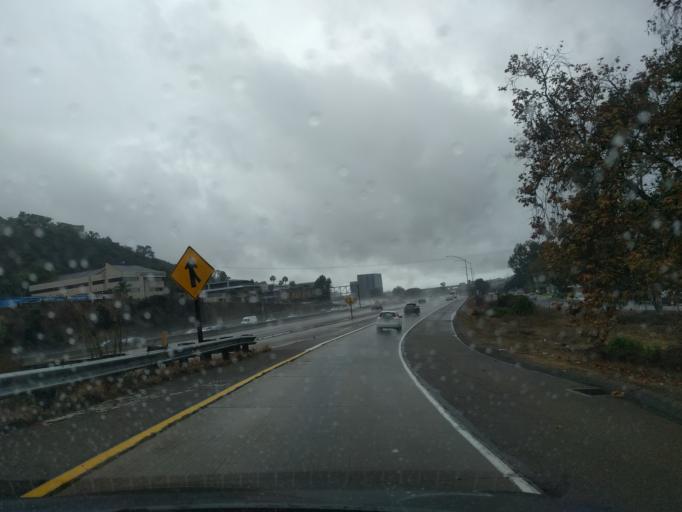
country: US
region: California
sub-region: San Diego County
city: San Diego
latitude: 32.7791
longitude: -117.1149
